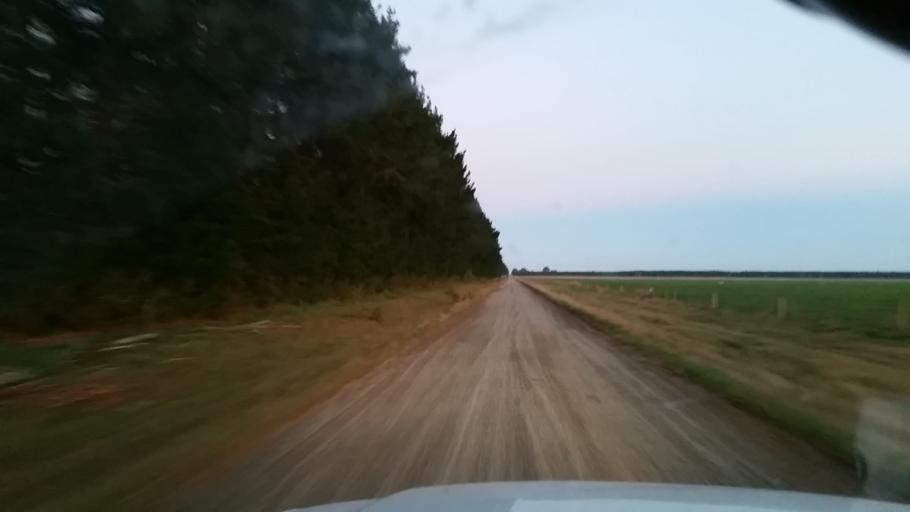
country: NZ
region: Canterbury
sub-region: Ashburton District
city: Tinwald
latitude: -43.9531
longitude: 171.6185
